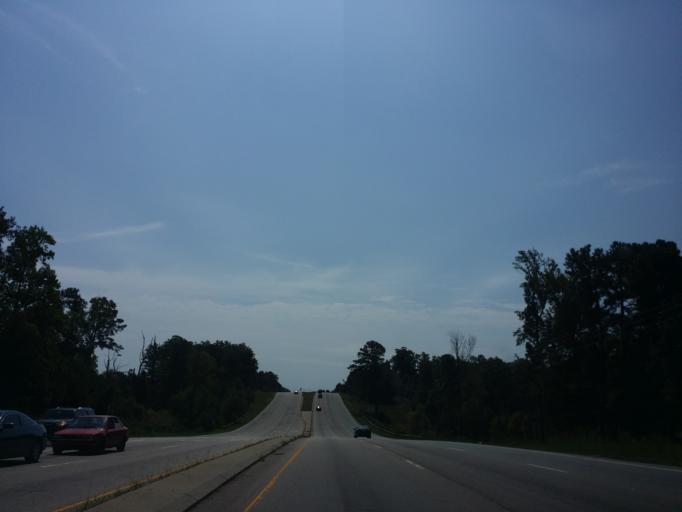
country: US
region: North Carolina
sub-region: Wake County
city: Morrisville
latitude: 35.9172
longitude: -78.7888
